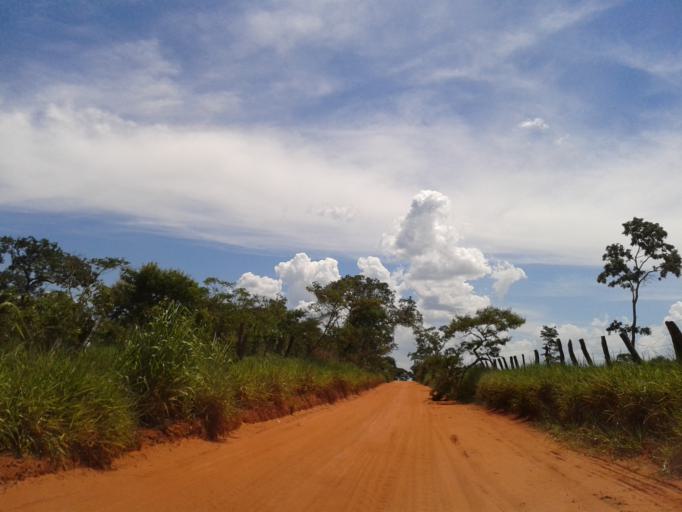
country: BR
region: Minas Gerais
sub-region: Santa Vitoria
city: Santa Vitoria
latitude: -19.1342
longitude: -50.5546
